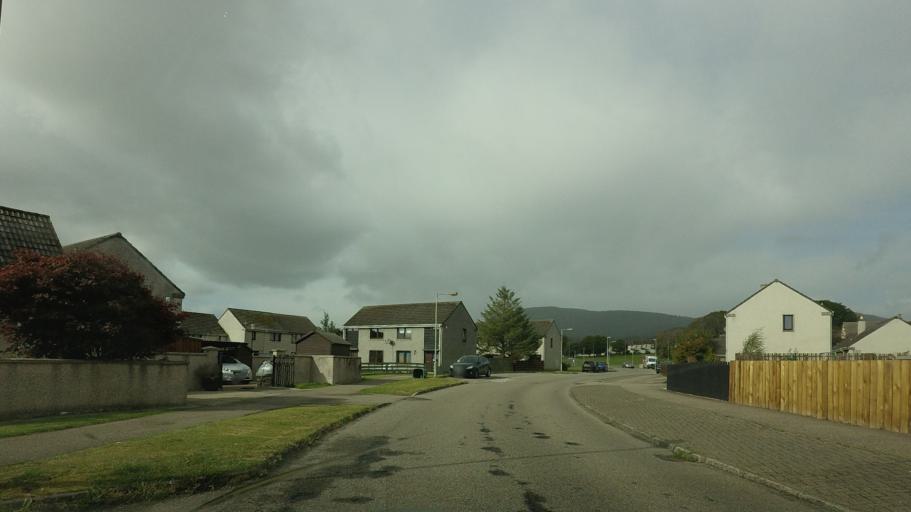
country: GB
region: Scotland
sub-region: Highland
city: Alness
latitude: 57.6946
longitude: -4.2698
